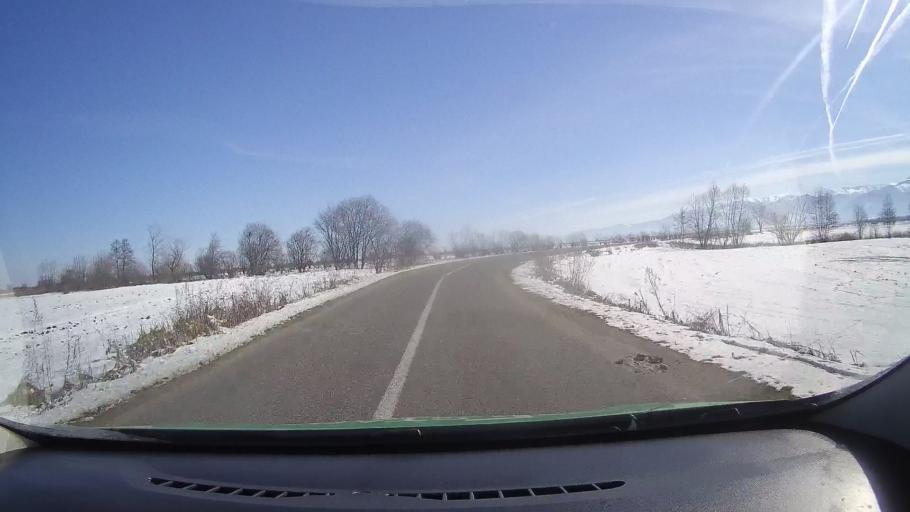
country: RO
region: Brasov
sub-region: Comuna Sambata de Sus
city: Sambata de Sus
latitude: 45.7473
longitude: 24.8408
